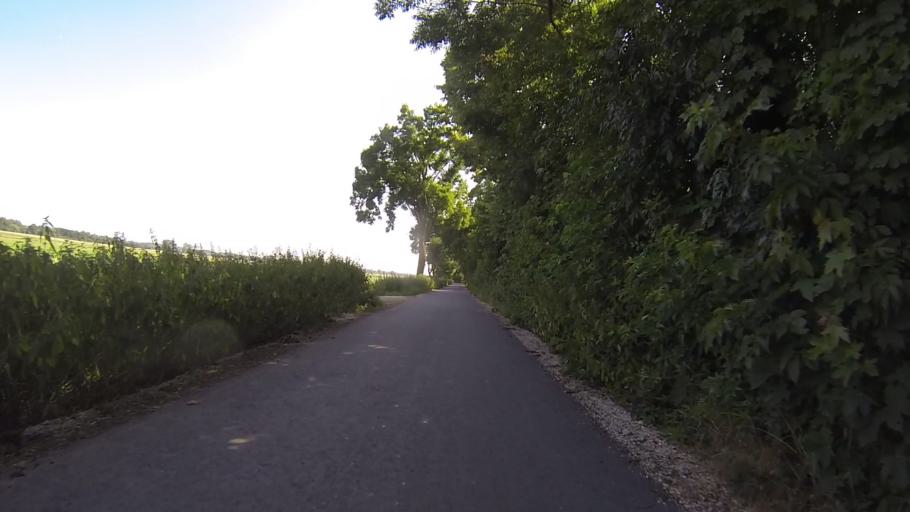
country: DE
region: Baden-Wuerttemberg
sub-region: Tuebingen Region
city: Erbach
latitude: 48.3507
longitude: 9.9218
